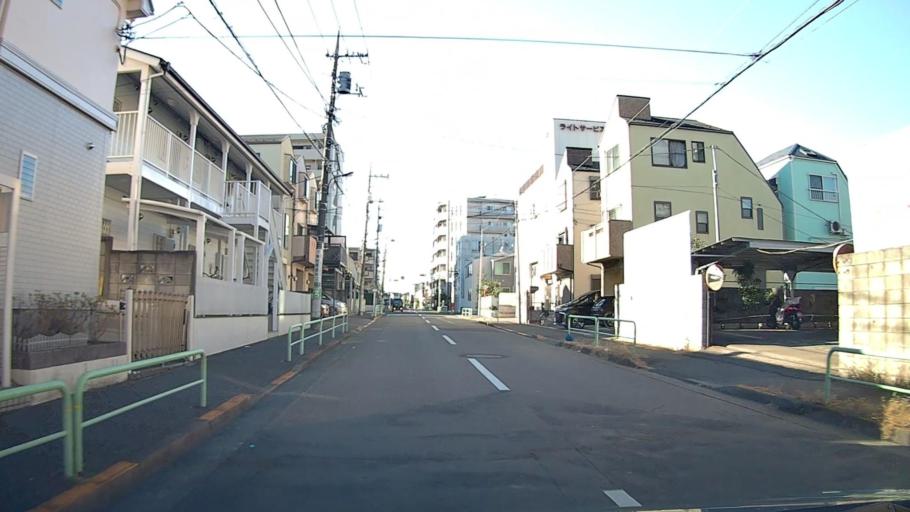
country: JP
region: Saitama
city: Wako
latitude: 35.7291
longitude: 139.6406
